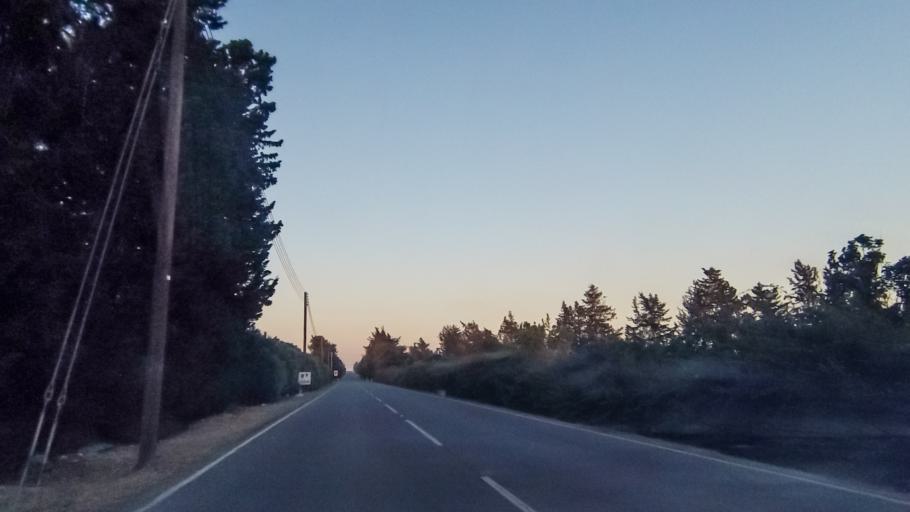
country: CY
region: Limassol
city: Erimi
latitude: 34.6605
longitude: 32.9032
